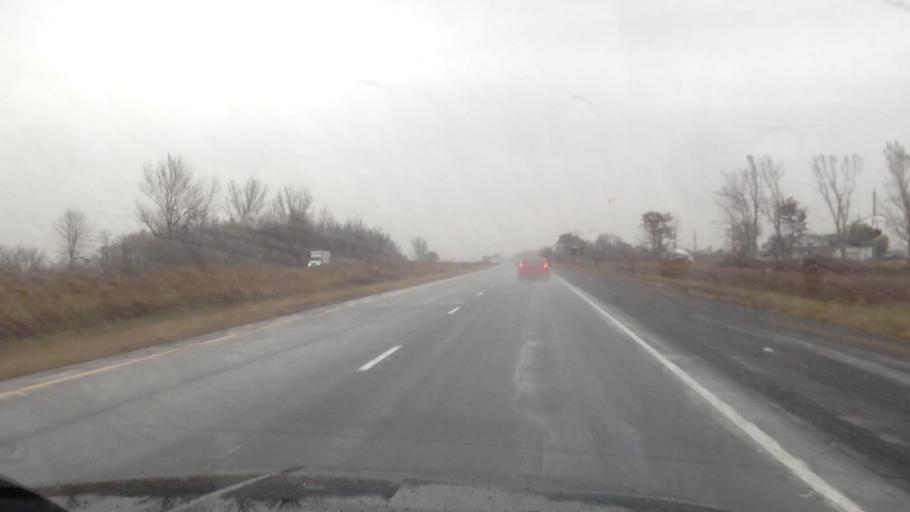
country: CA
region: Ontario
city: Casselman
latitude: 45.3123
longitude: -75.0332
